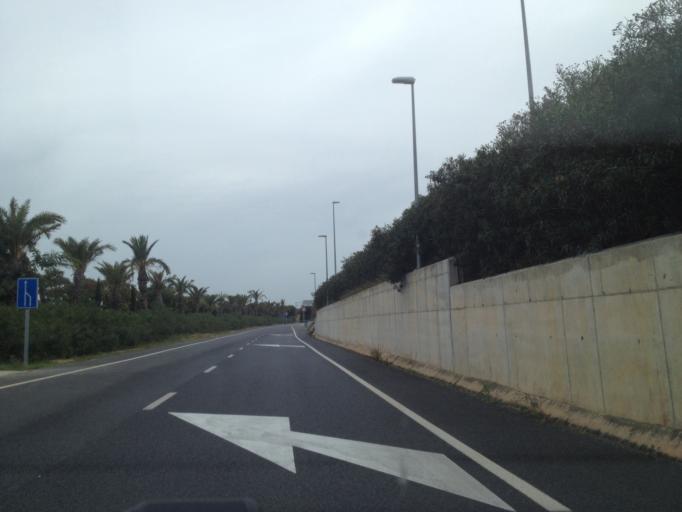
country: ES
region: Balearic Islands
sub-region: Illes Balears
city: s'Arenal
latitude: 39.5448
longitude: 2.7237
